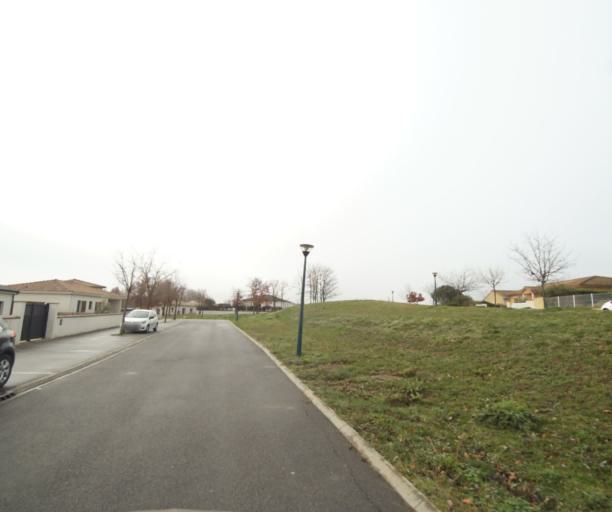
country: FR
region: Midi-Pyrenees
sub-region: Departement de la Haute-Garonne
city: Villemur-sur-Tarn
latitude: 43.8546
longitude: 1.4817
